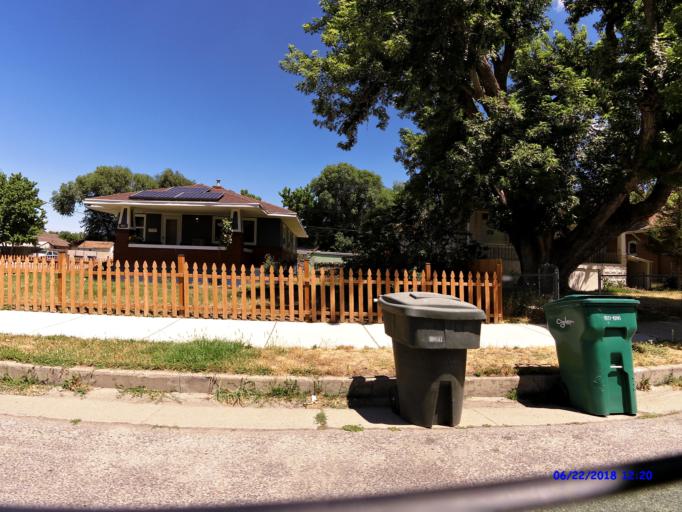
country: US
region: Utah
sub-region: Weber County
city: Ogden
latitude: 41.2378
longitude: -111.9683
